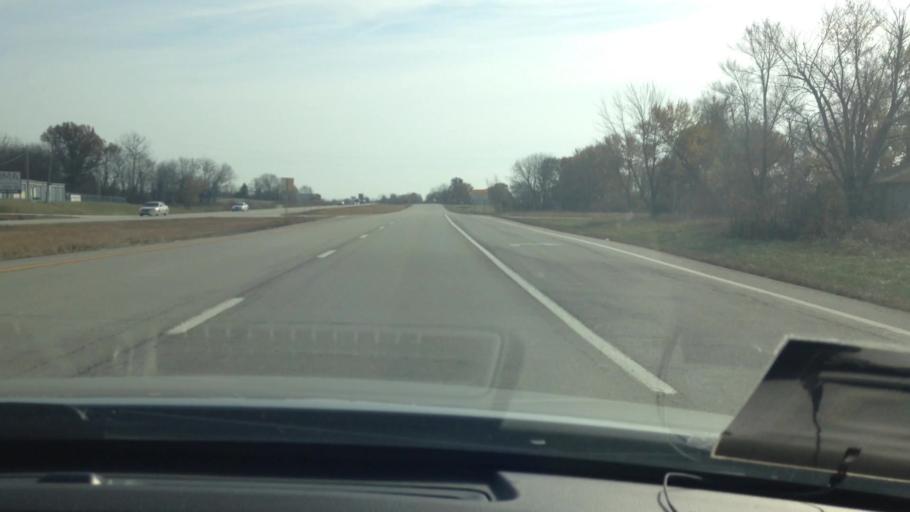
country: US
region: Missouri
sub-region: Cass County
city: Harrisonville
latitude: 38.6162
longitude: -94.3304
